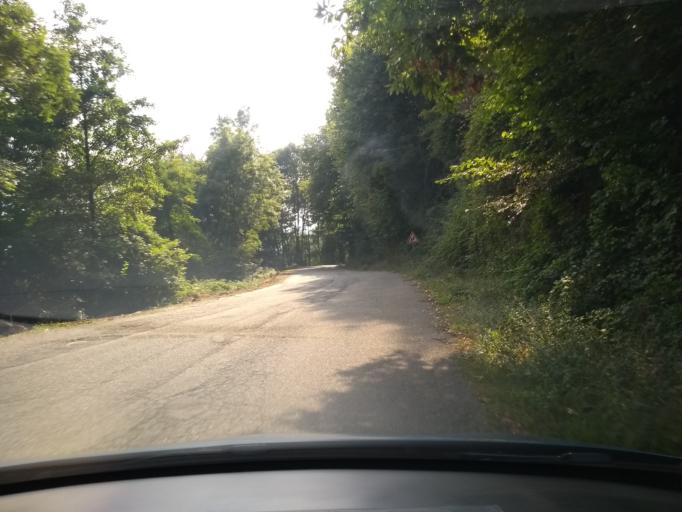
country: IT
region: Piedmont
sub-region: Provincia di Torino
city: Corio
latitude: 45.3065
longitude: 7.5110
